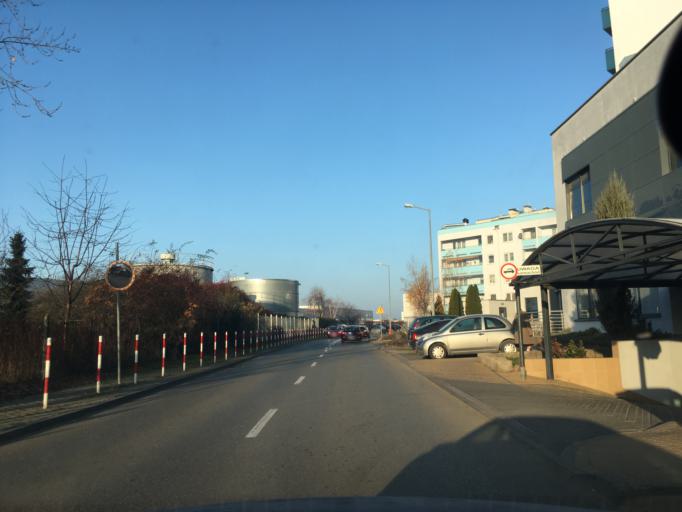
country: PL
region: Masovian Voivodeship
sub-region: Powiat piaseczynski
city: Piaseczno
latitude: 52.0776
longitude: 21.0097
